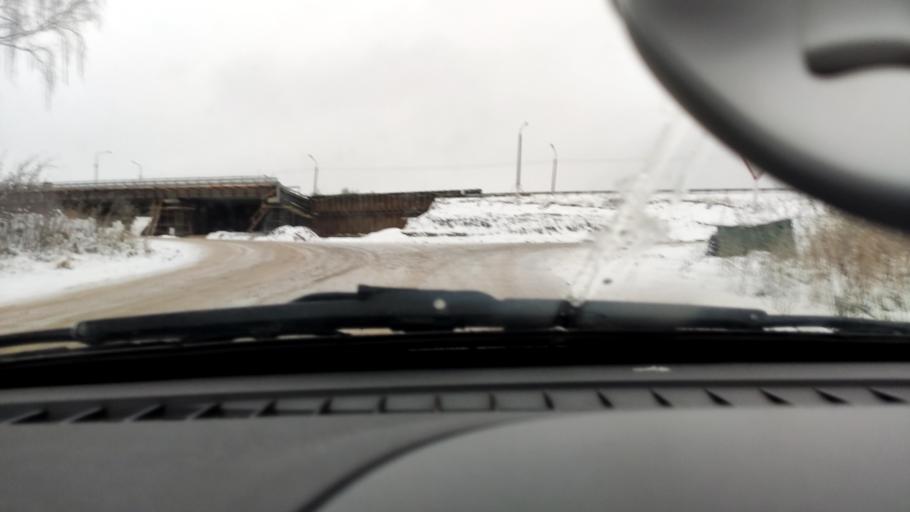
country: RU
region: Perm
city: Polazna
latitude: 58.1796
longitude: 56.4124
